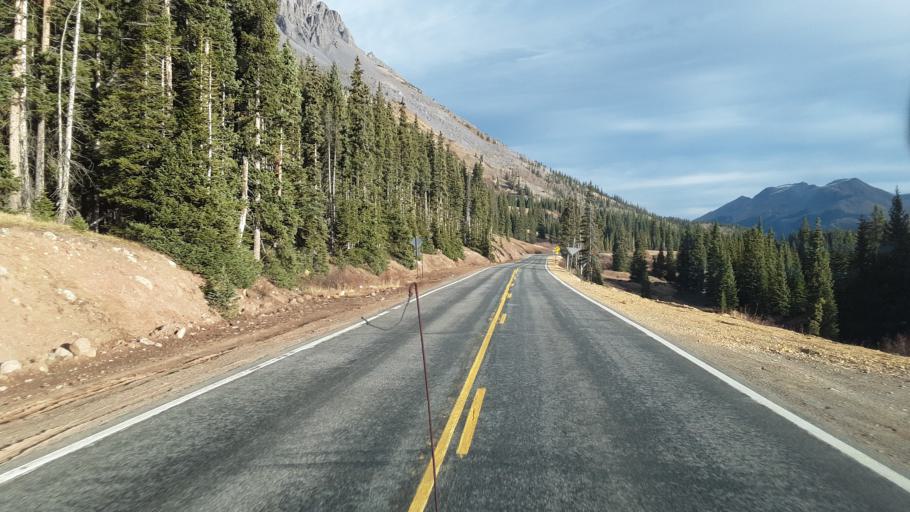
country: US
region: Colorado
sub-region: San Juan County
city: Silverton
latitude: 37.7587
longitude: -107.6805
